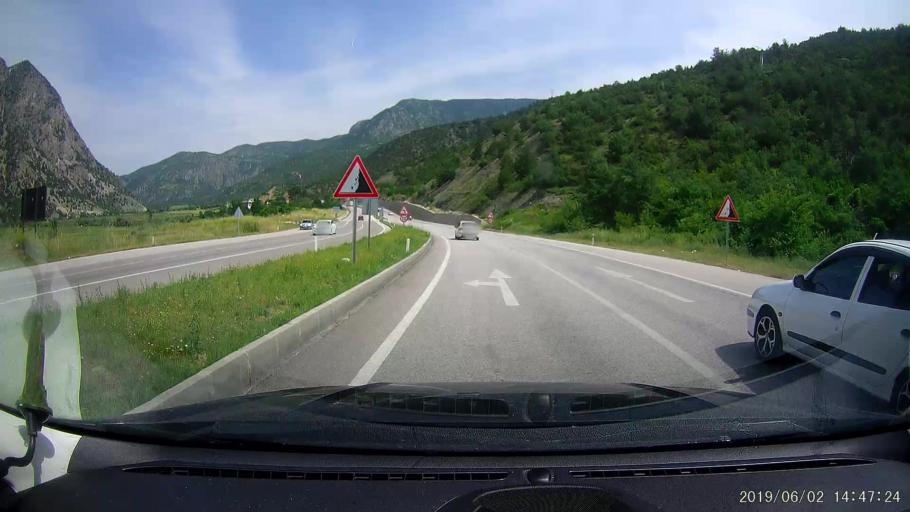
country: TR
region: Corum
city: Hacihamza
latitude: 41.0690
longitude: 34.4595
